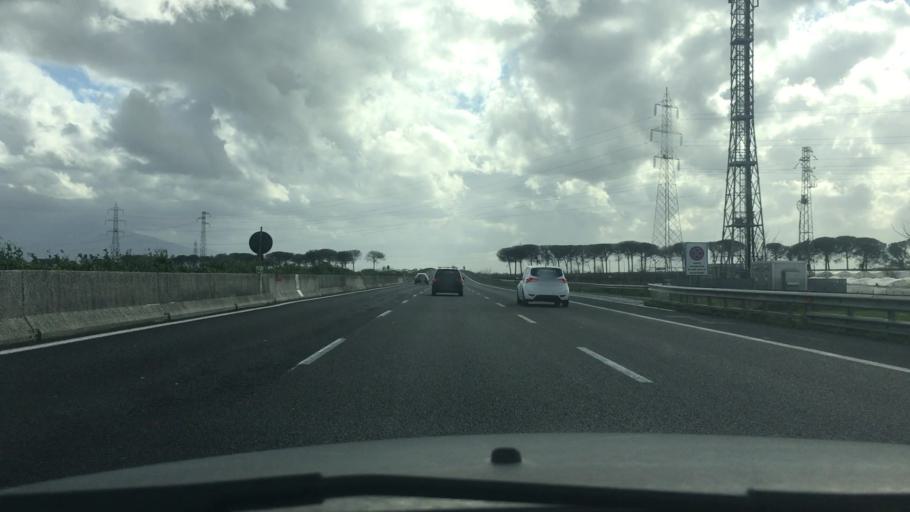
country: IT
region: Campania
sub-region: Provincia di Napoli
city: Pascarola
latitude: 40.9910
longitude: 14.3247
